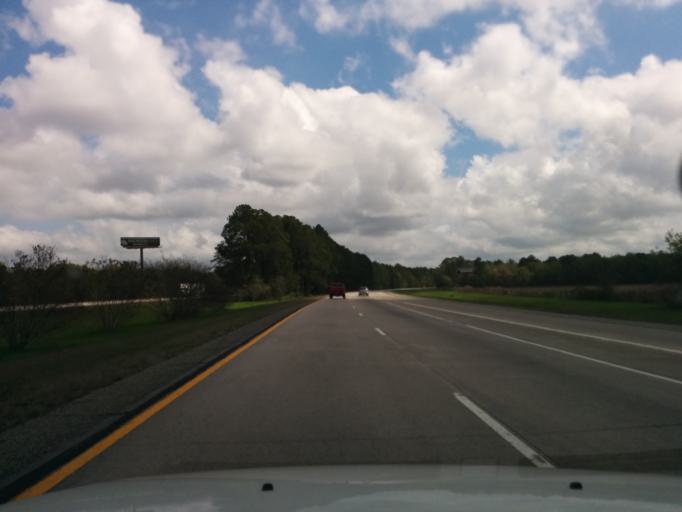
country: US
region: Georgia
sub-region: Bulloch County
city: Brooklet
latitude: 32.2550
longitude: -81.7062
